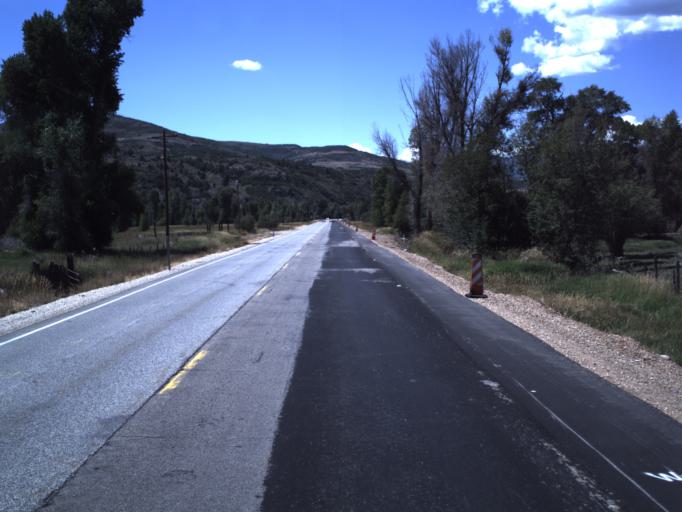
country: US
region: Utah
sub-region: Summit County
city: Francis
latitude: 40.6048
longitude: -111.3196
